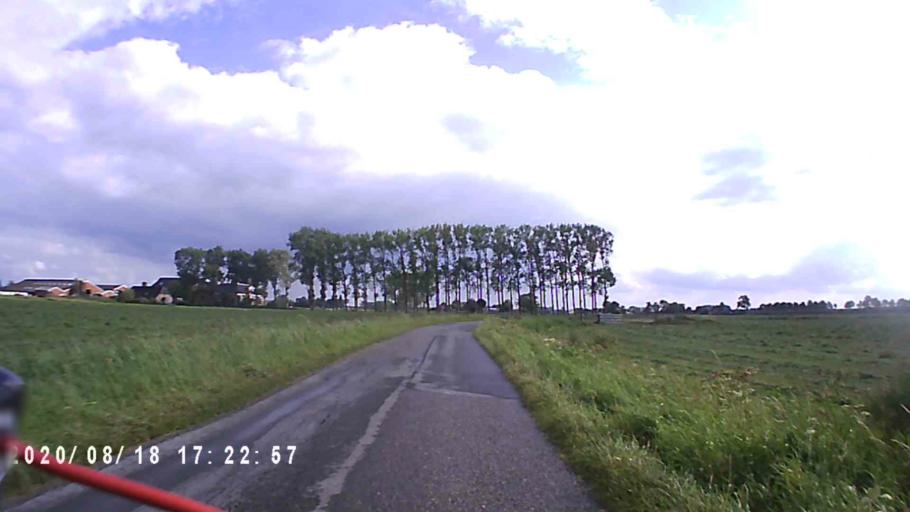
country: NL
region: Groningen
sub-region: Gemeente Zuidhorn
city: Aduard
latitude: 53.2494
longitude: 6.4883
